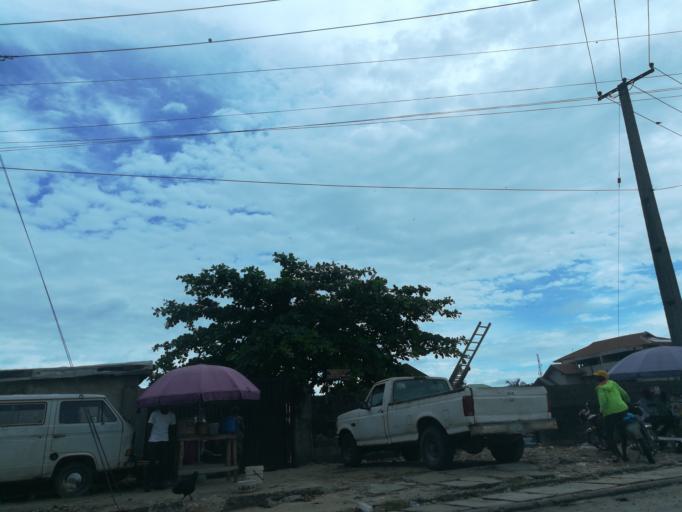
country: NG
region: Lagos
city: Ikoyi
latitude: 6.4426
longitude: 3.4724
